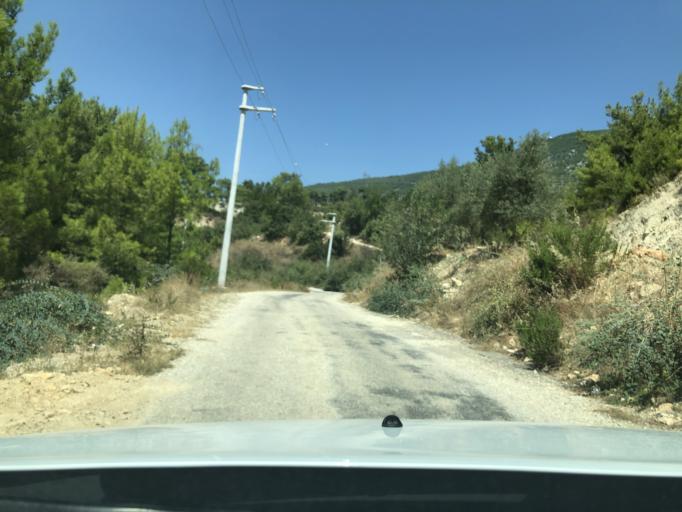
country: TR
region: Antalya
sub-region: Manavgat
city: Manavgat
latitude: 36.8701
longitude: 31.5558
